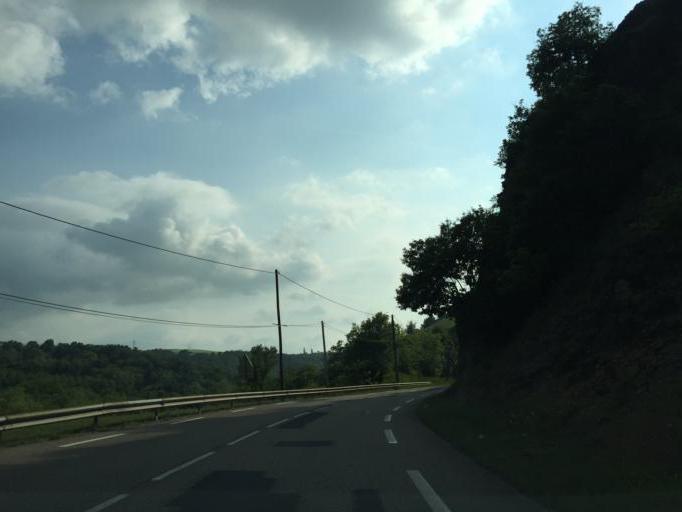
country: FR
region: Rhone-Alpes
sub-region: Departement de la Loire
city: Chateauneuf
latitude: 45.5491
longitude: 4.6732
